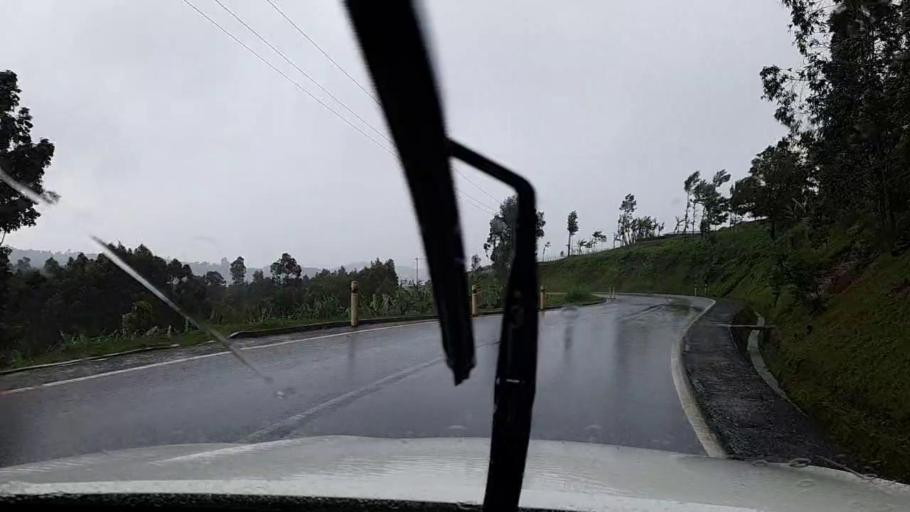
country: RW
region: Western Province
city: Cyangugu
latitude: -2.4621
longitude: 28.9911
